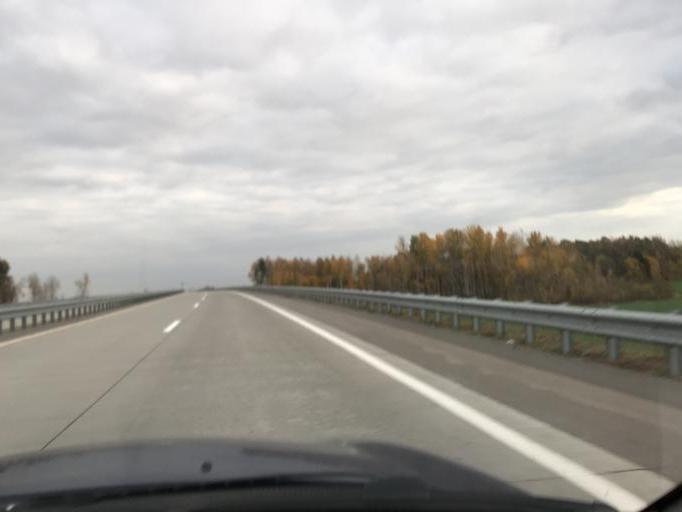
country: BY
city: Fanipol
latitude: 53.7679
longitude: 27.3665
